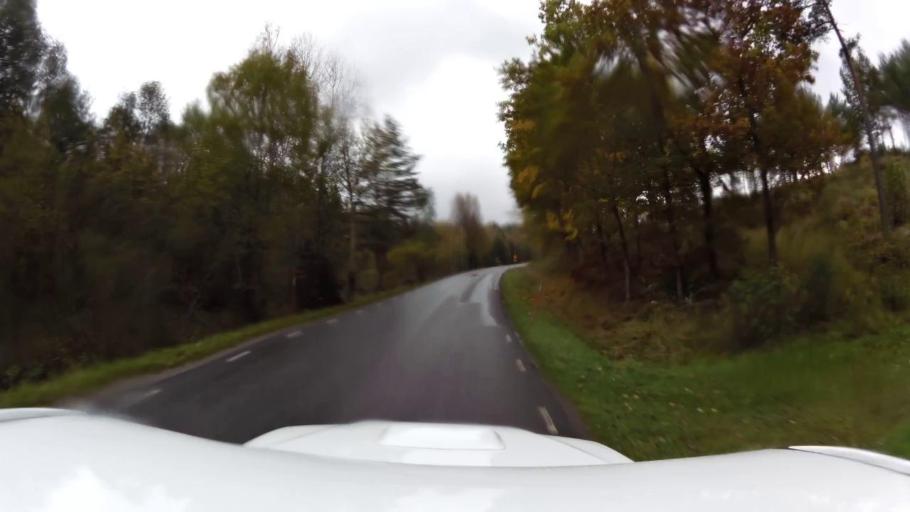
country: SE
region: OEstergoetland
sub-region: Linkopings Kommun
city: Ljungsbro
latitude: 58.5217
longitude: 15.5246
